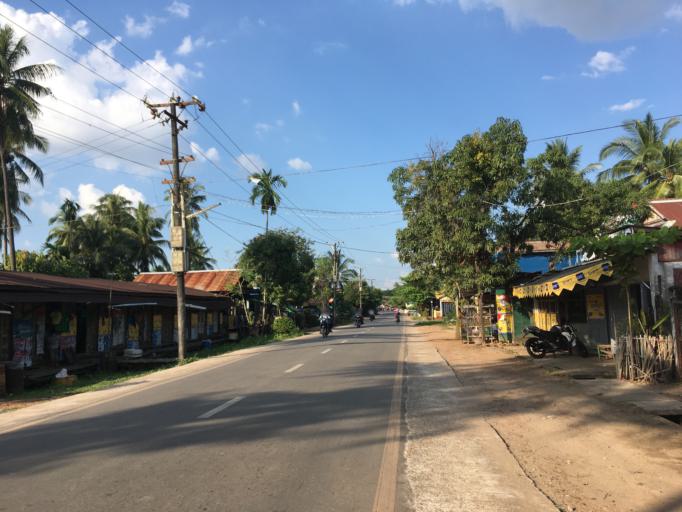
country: MM
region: Mon
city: Mawlamyine
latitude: 16.4525
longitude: 97.6251
